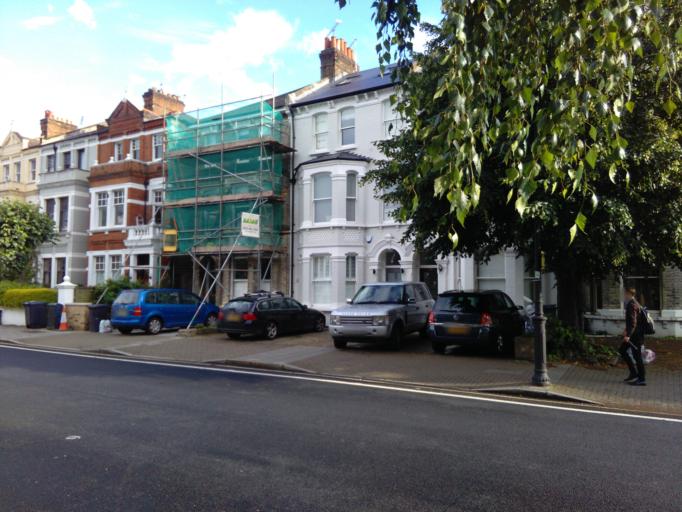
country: GB
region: England
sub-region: Greater London
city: Kennington
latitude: 51.4818
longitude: -0.1211
